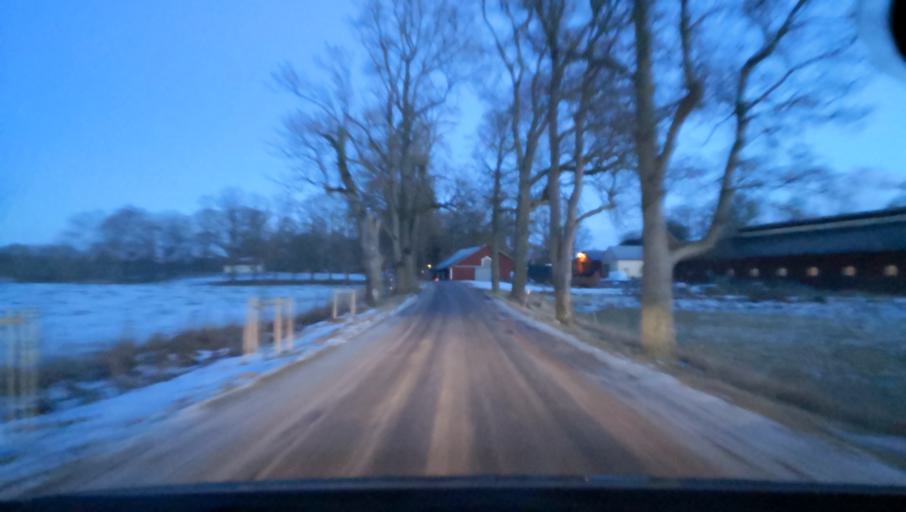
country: SE
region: Soedermanland
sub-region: Katrineholms Kommun
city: Katrineholm
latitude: 59.0852
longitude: 16.3104
